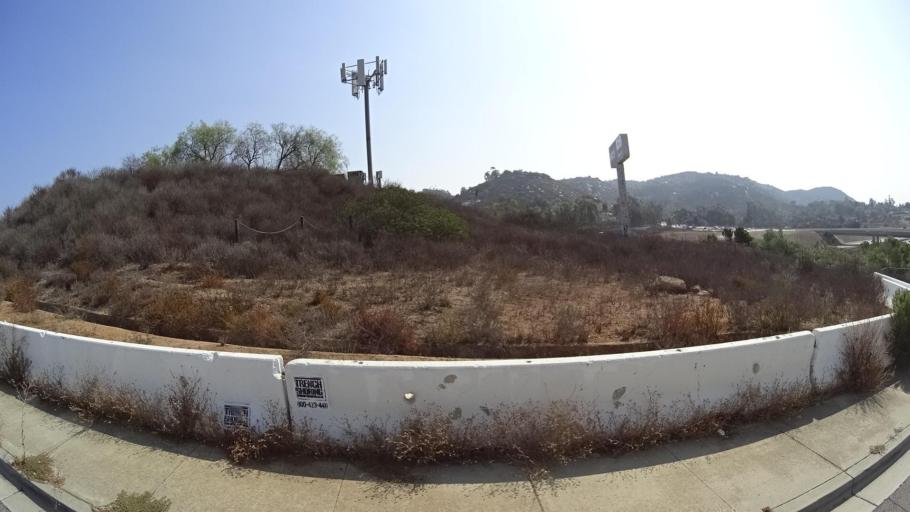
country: US
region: California
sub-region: San Diego County
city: Hidden Meadows
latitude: 33.1990
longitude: -117.1285
